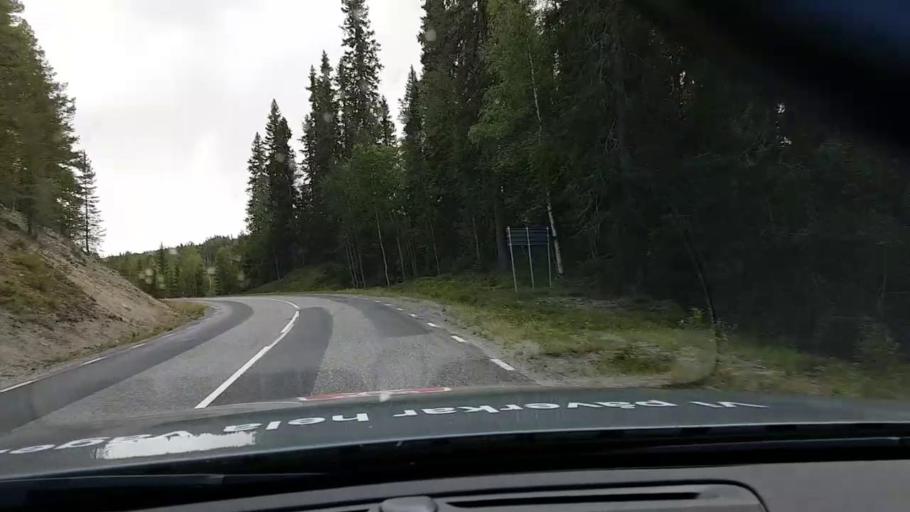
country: SE
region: Vaesterbotten
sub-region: Asele Kommun
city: Asele
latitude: 63.8379
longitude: 17.4344
